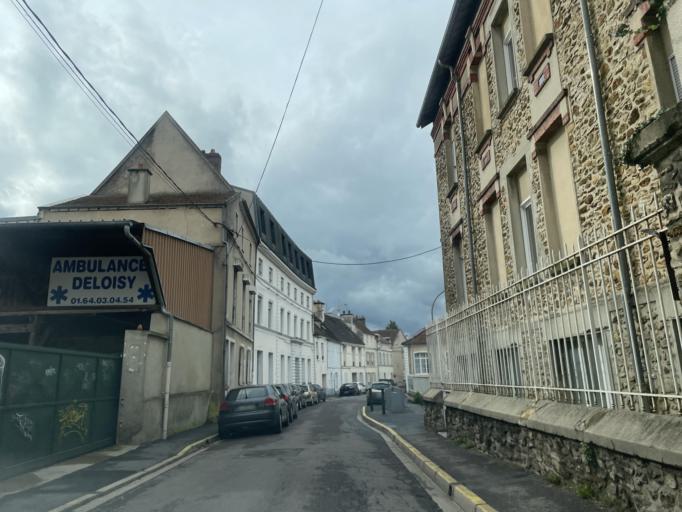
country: FR
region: Ile-de-France
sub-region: Departement de Seine-et-Marne
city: Coulommiers
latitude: 48.8141
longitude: 3.0830
